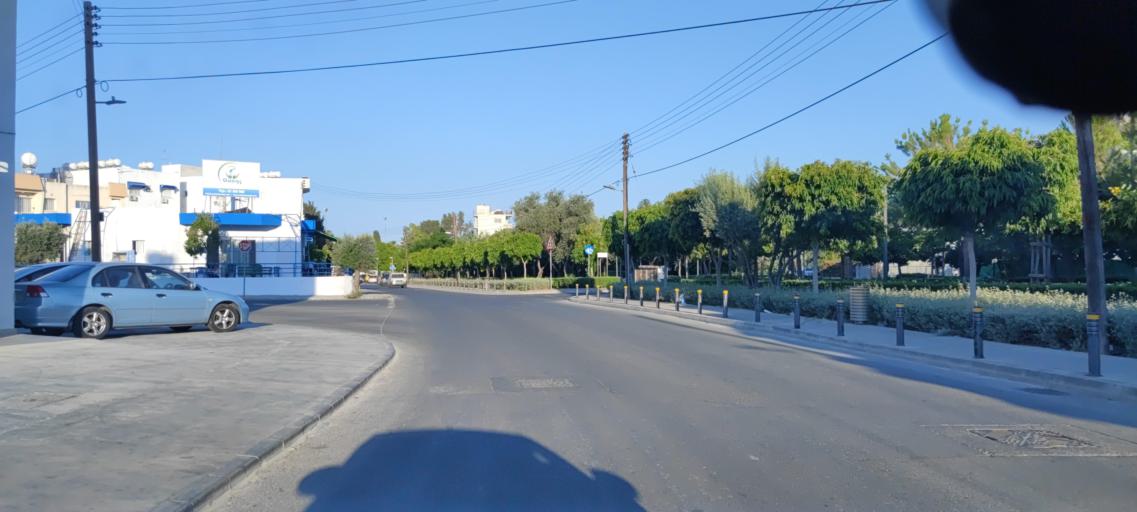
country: CY
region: Limassol
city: Limassol
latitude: 34.6770
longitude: 33.0311
